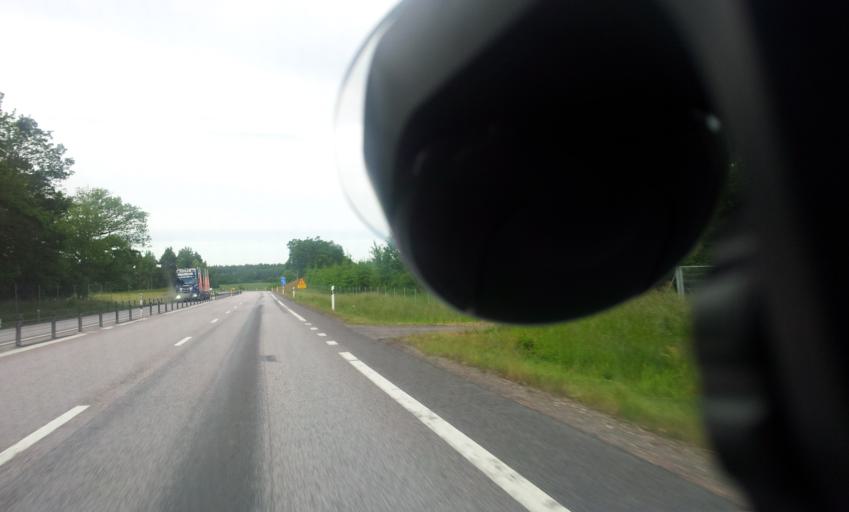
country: SE
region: Kalmar
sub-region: Monsteras Kommun
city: Moensteras
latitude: 57.0950
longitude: 16.4904
